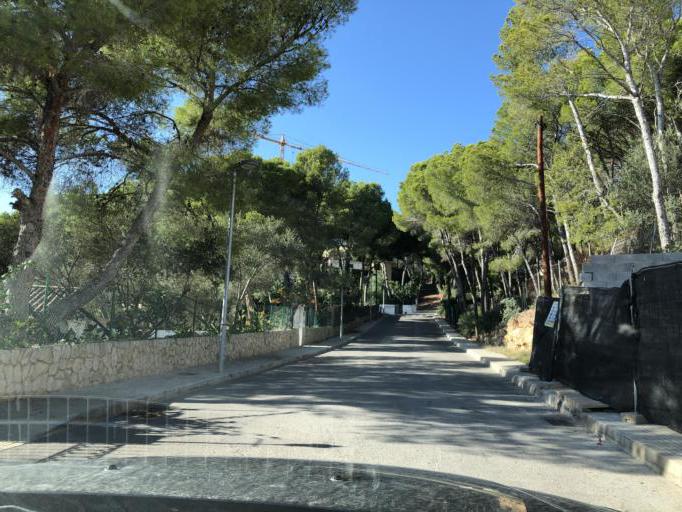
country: ES
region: Balearic Islands
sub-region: Illes Balears
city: Camp de Mar
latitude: 39.5395
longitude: 2.4147
